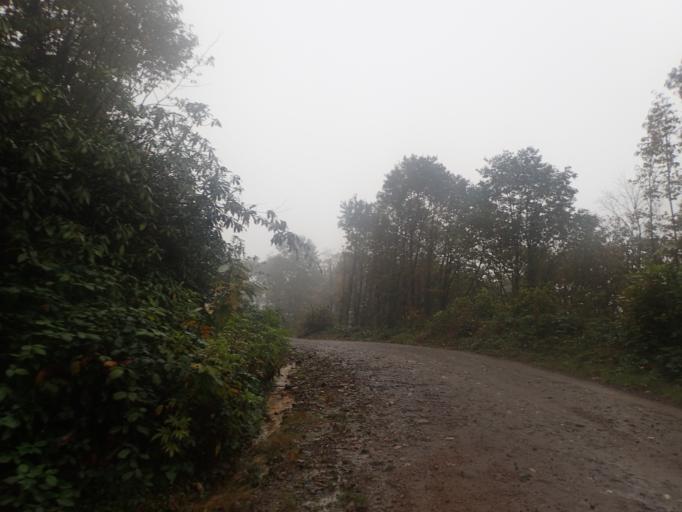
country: TR
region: Ordu
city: Persembe
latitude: 41.0195
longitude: 37.6983
